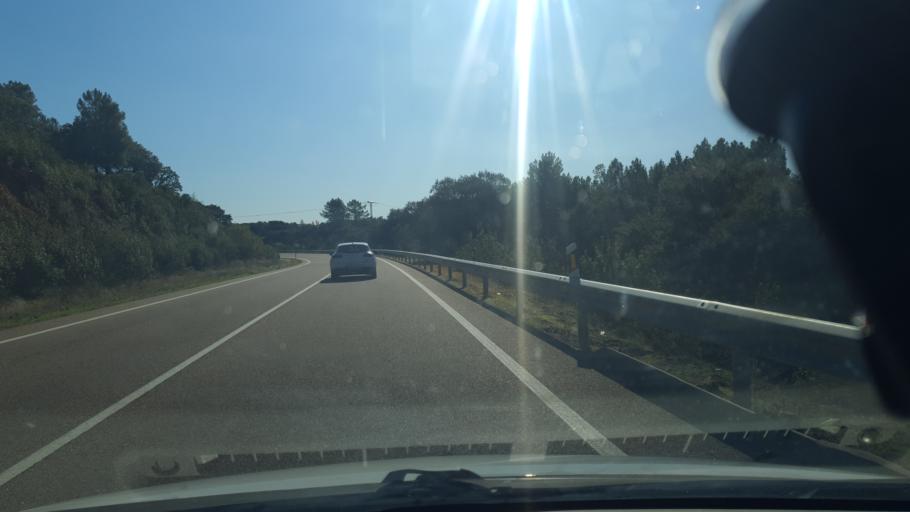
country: ES
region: Castille and Leon
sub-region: Provincia de Avila
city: Poyales del Hoyo
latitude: 40.1653
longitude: -5.1205
